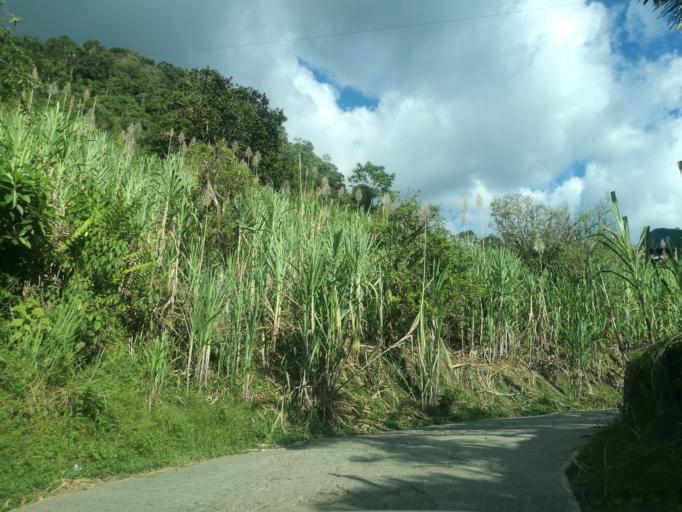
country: CO
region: Boyaca
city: Maripi
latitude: 5.5514
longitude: -74.0018
